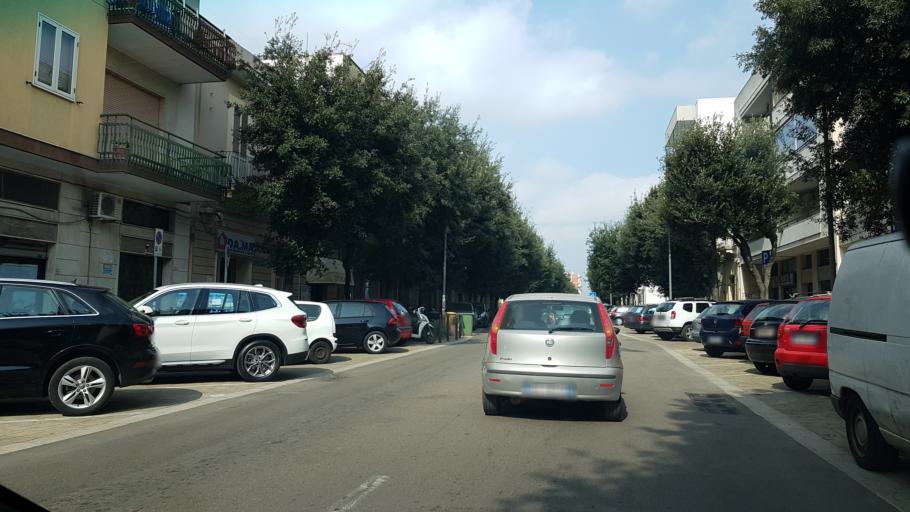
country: IT
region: Apulia
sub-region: Provincia di Lecce
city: Castromediano
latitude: 40.3395
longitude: 18.1768
